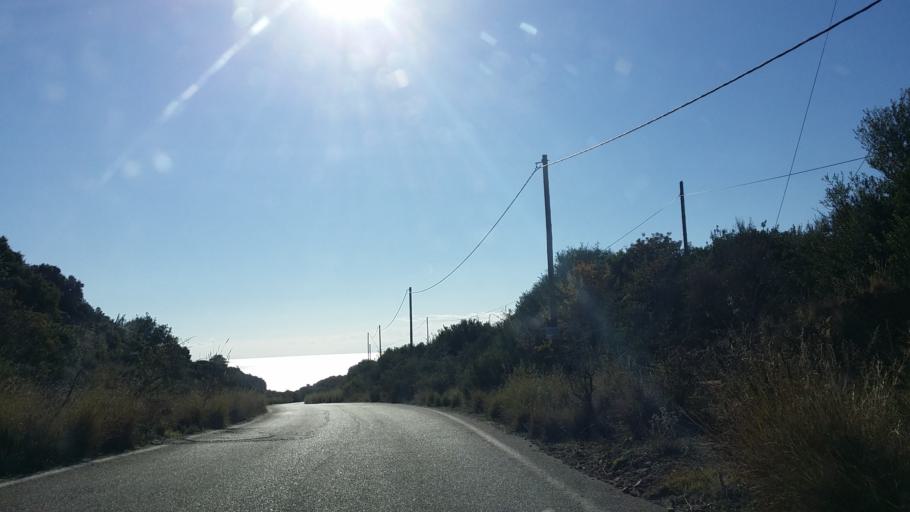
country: GR
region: West Greece
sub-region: Nomos Aitolias kai Akarnanias
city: Archontochorion
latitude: 38.6556
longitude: 20.9922
